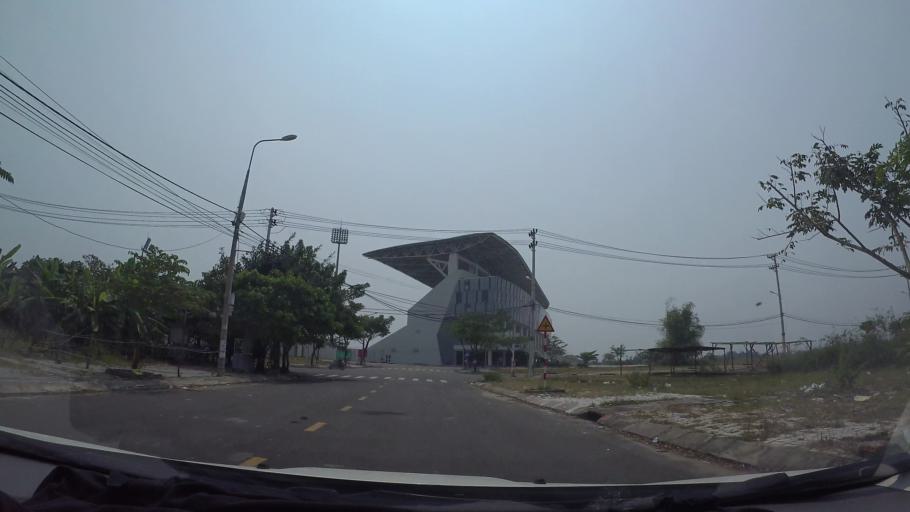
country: VN
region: Da Nang
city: Cam Le
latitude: 16.0005
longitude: 108.2221
